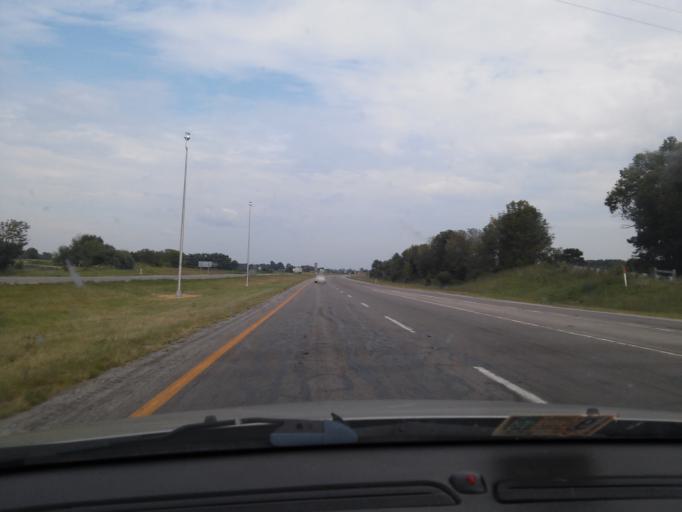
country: US
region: Ohio
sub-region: Fayette County
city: Washington Court House
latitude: 39.5479
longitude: -83.4849
